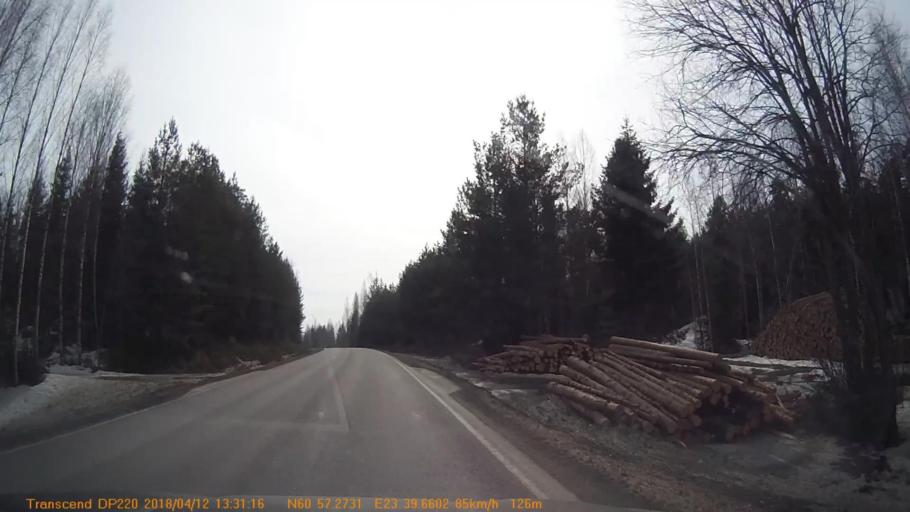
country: FI
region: Haeme
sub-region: Forssa
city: Forssa
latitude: 60.9544
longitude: 23.6609
